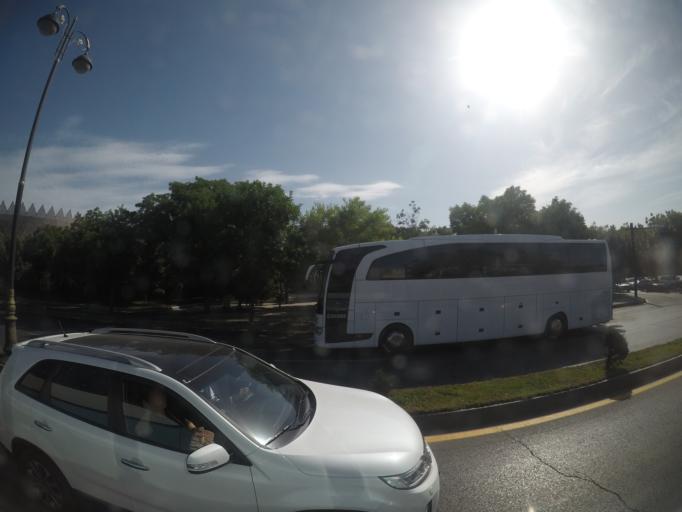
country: AZ
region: Baki
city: Badamdar
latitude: 40.3896
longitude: 49.8253
